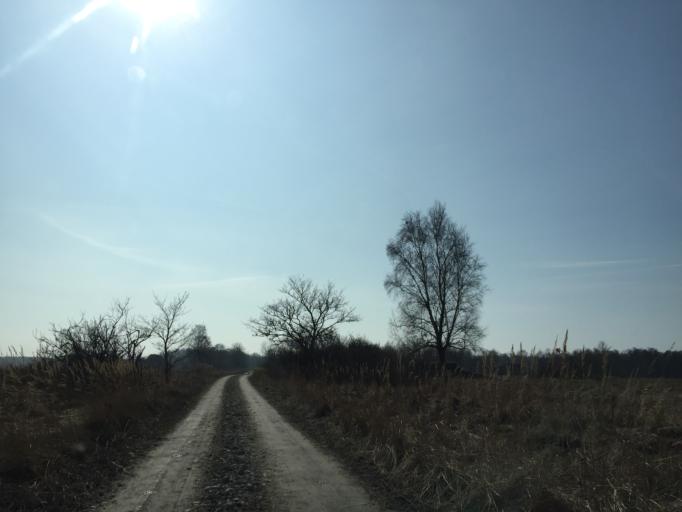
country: LV
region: Dundaga
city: Dundaga
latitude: 57.9301
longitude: 22.0633
